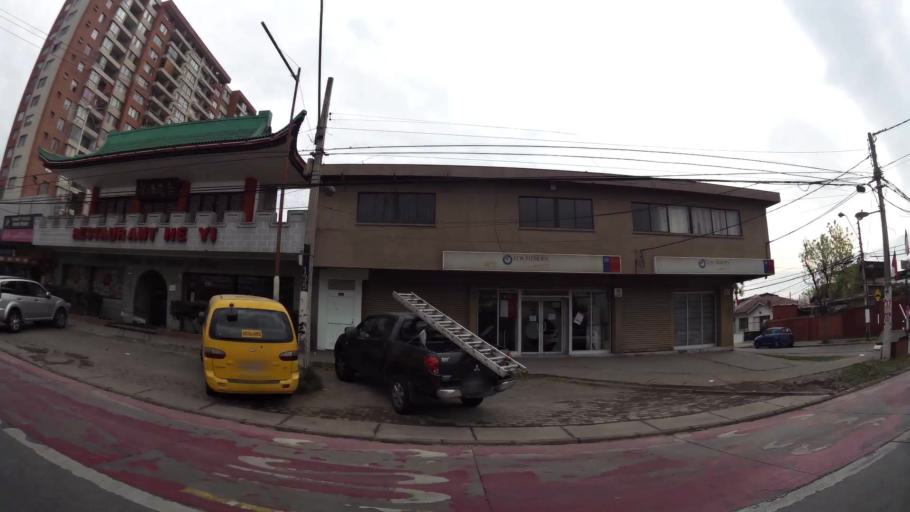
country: CL
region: Santiago Metropolitan
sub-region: Provincia de Santiago
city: Villa Presidente Frei, Nunoa, Santiago, Chile
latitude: -33.4967
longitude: -70.5983
